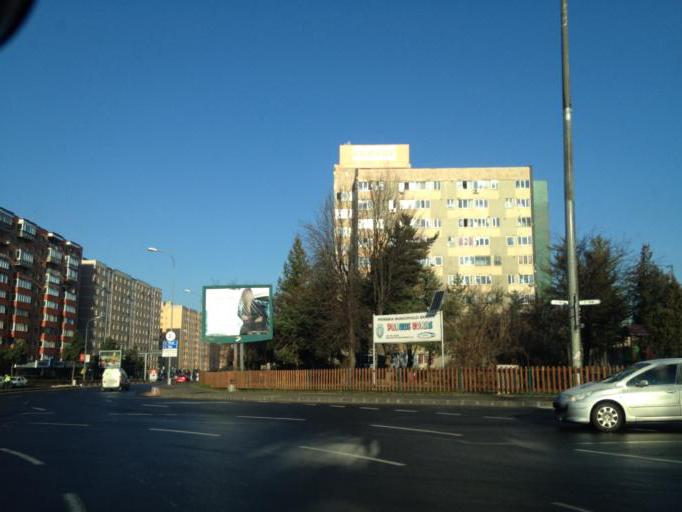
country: RO
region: Brasov
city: Brasov
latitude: 45.6344
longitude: 25.6345
